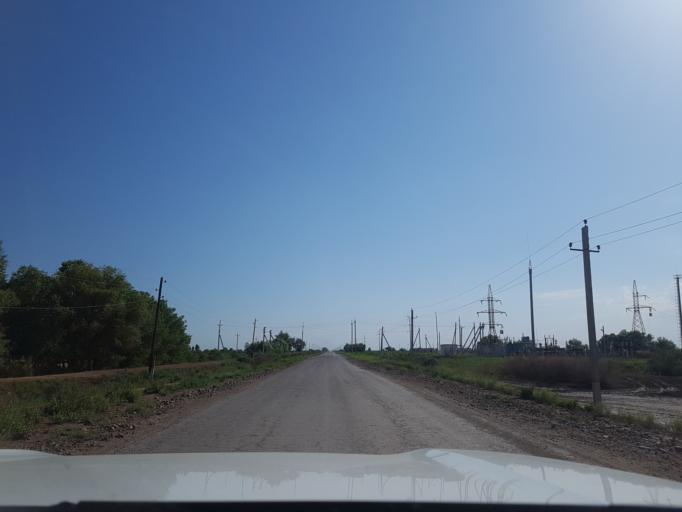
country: TM
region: Dasoguz
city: Koeneuergench
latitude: 42.0975
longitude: 58.8982
